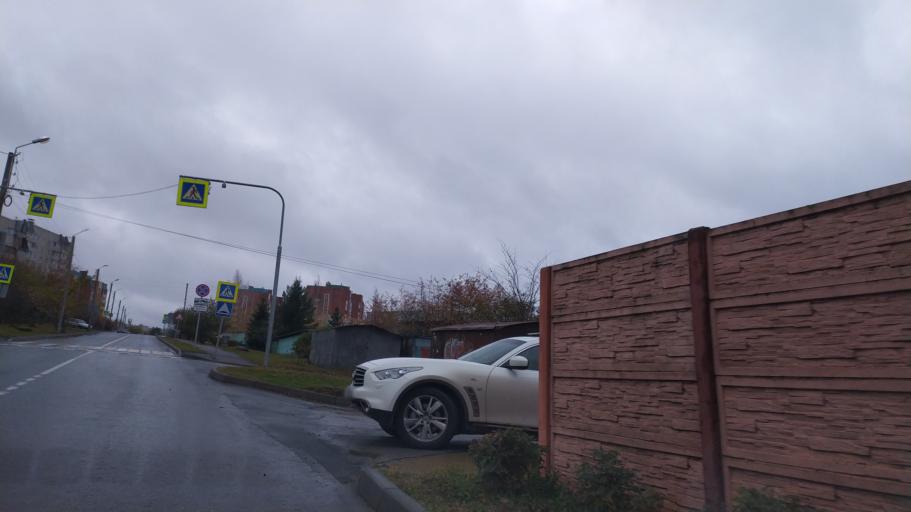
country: RU
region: Chuvashia
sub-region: Cheboksarskiy Rayon
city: Cheboksary
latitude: 56.1462
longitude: 47.1618
